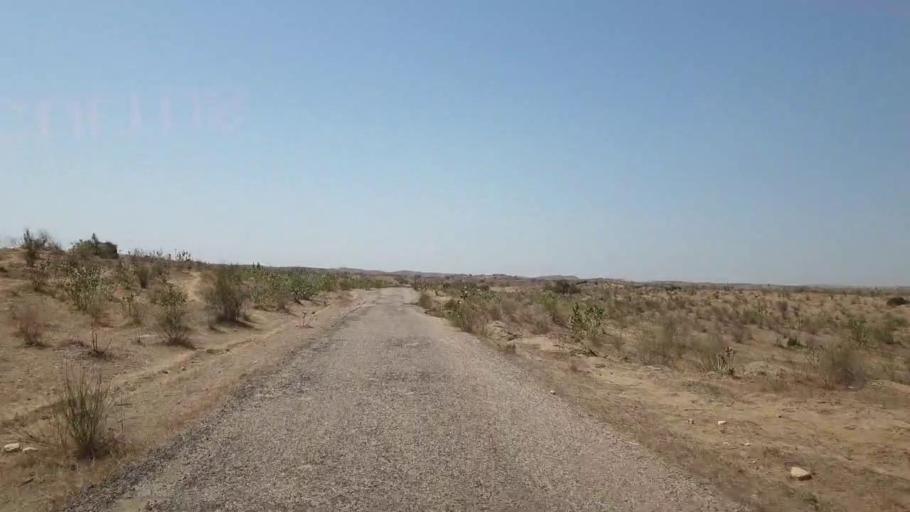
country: PK
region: Sindh
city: Nabisar
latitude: 25.1369
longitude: 69.9201
